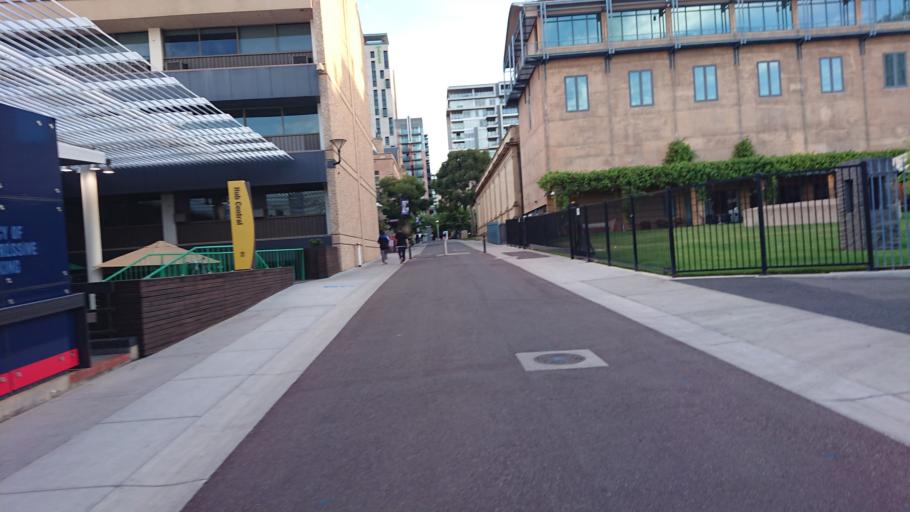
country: AU
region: South Australia
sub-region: Adelaide
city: Adelaide
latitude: -34.9197
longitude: 138.6042
